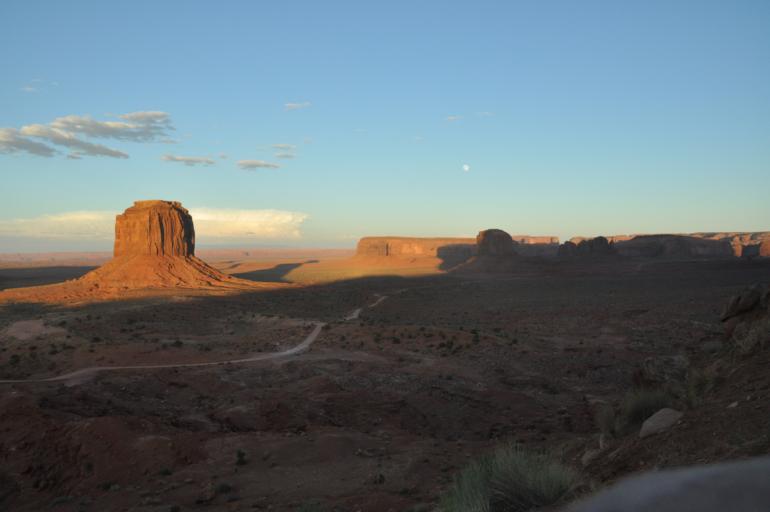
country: US
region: Arizona
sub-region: Navajo County
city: Kayenta
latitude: 36.9827
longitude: -110.1116
